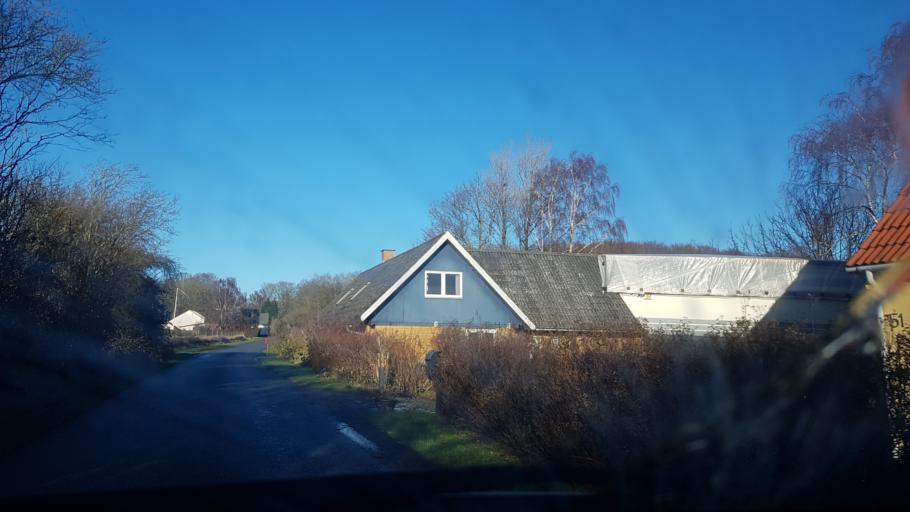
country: DK
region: South Denmark
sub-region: Fredericia Kommune
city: Taulov
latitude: 55.5206
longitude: 9.6514
